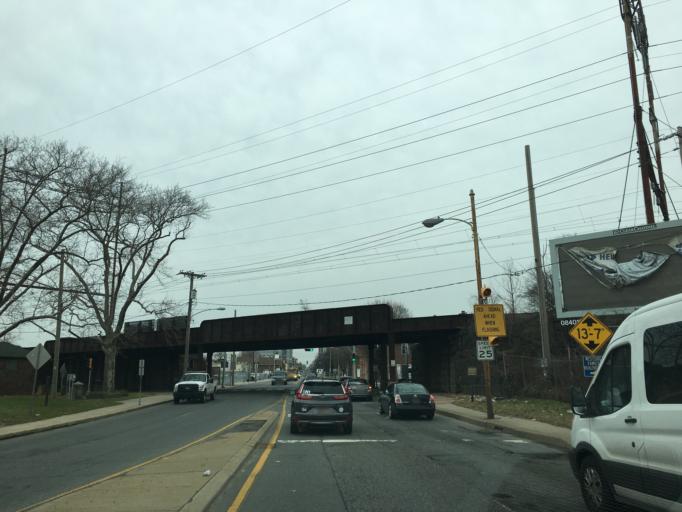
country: US
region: Delaware
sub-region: New Castle County
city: Wilmington
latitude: 39.7367
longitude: -75.5420
